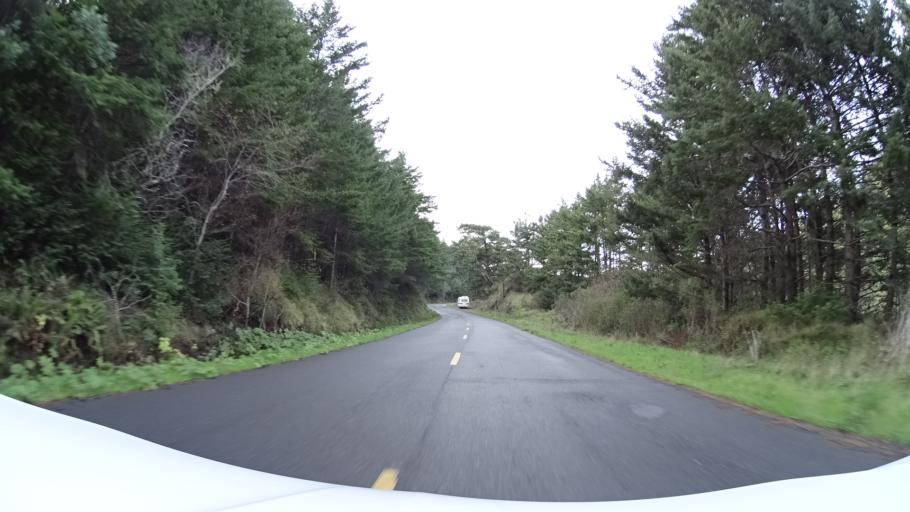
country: US
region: California
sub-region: Humboldt County
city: Ferndale
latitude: 40.3468
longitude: -124.3517
